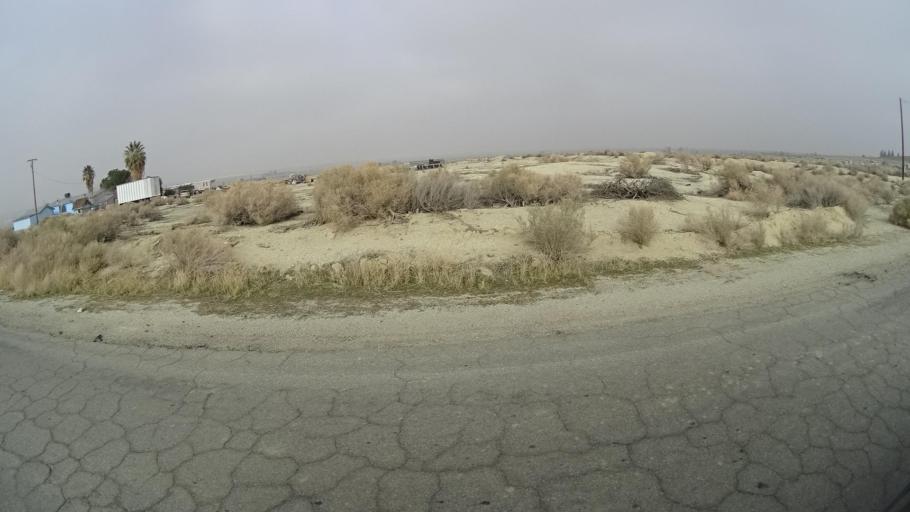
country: US
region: California
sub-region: Kern County
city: Maricopa
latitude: 35.0376
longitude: -119.3658
